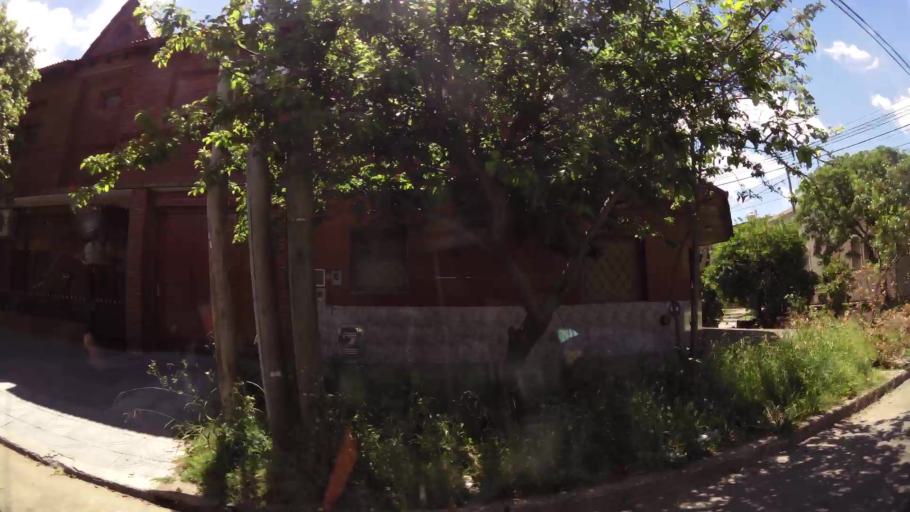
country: AR
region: Buenos Aires
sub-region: Partido de Lanus
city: Lanus
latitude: -34.7025
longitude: -58.4156
